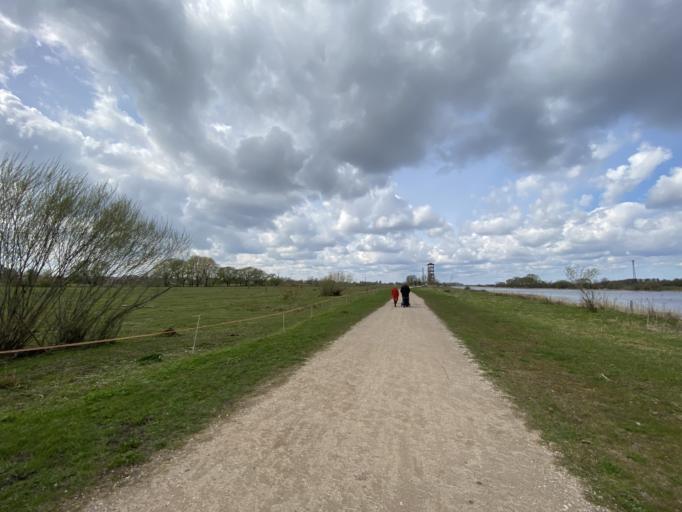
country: LV
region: Jelgava
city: Jelgava
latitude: 56.6610
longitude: 23.7284
